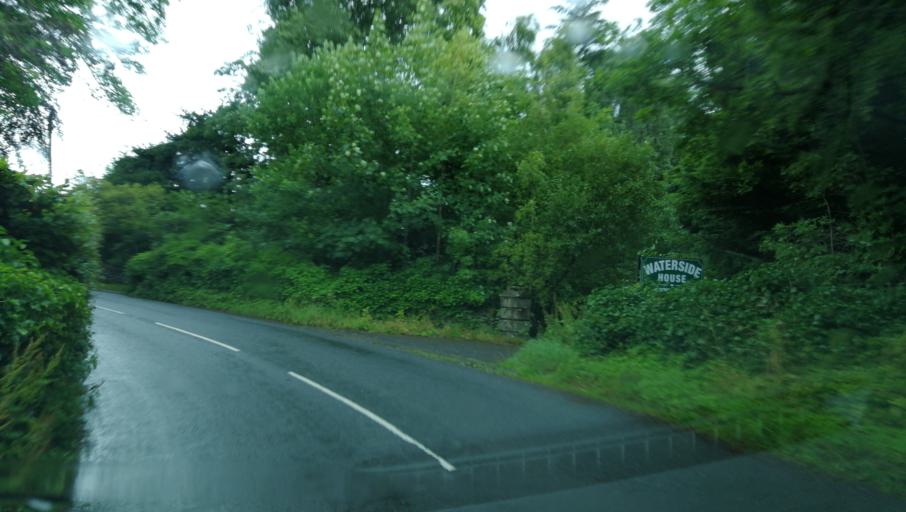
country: GB
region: England
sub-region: Cumbria
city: Penrith
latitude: 54.5938
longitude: -2.8585
